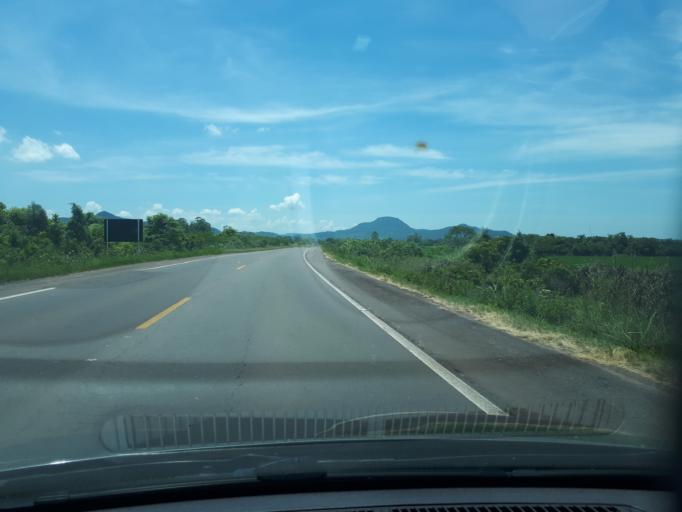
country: BR
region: Rio Grande do Sul
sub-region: Candelaria
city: Candelaria
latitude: -29.7296
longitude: -52.9418
